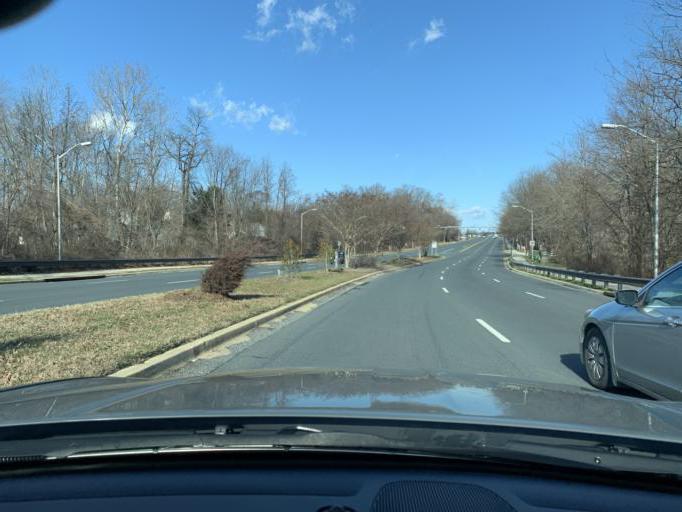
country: US
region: Maryland
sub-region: Prince George's County
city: Peppermill Village
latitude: 38.8996
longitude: -76.8660
